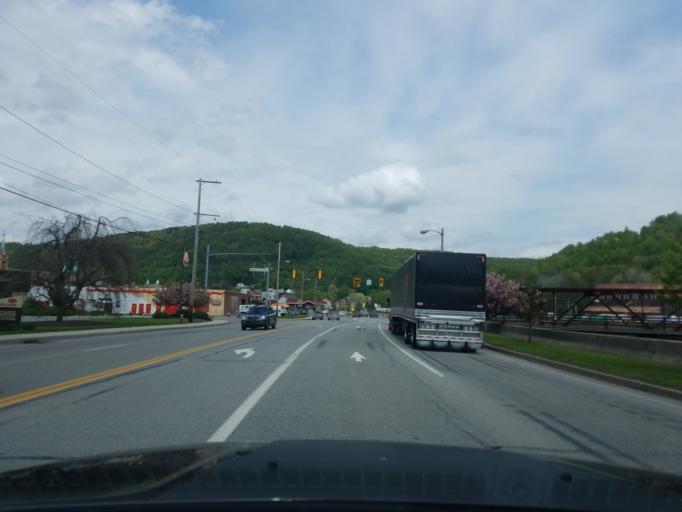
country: US
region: Pennsylvania
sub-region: Cambria County
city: Johnstown
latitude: 40.3362
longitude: -78.9255
